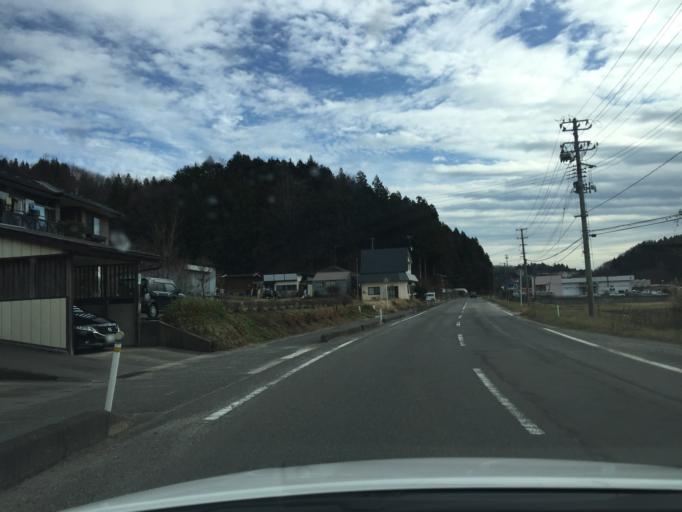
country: JP
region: Fukushima
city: Funehikimachi-funehiki
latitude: 37.2876
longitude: 140.6135
